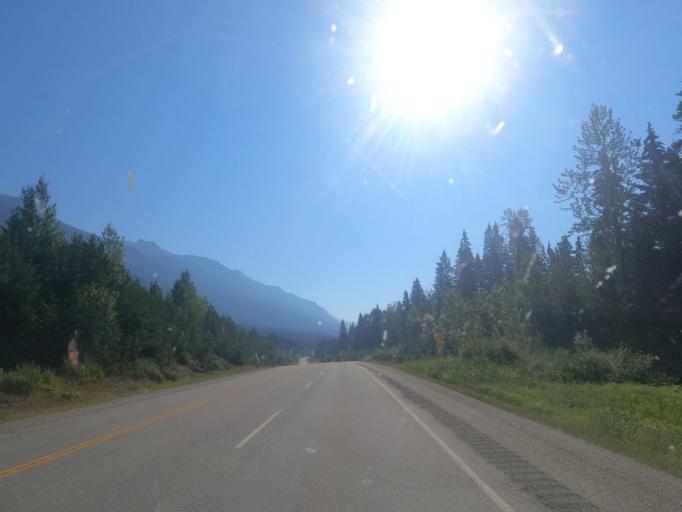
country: CA
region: Alberta
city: Grande Cache
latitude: 53.0032
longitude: -119.0467
